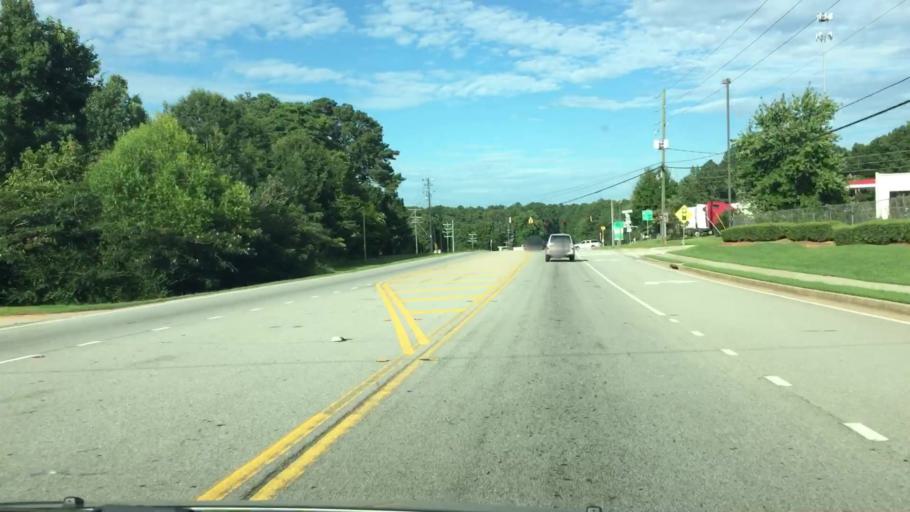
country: US
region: Georgia
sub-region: Henry County
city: Stockbridge
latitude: 33.5844
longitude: -84.1512
